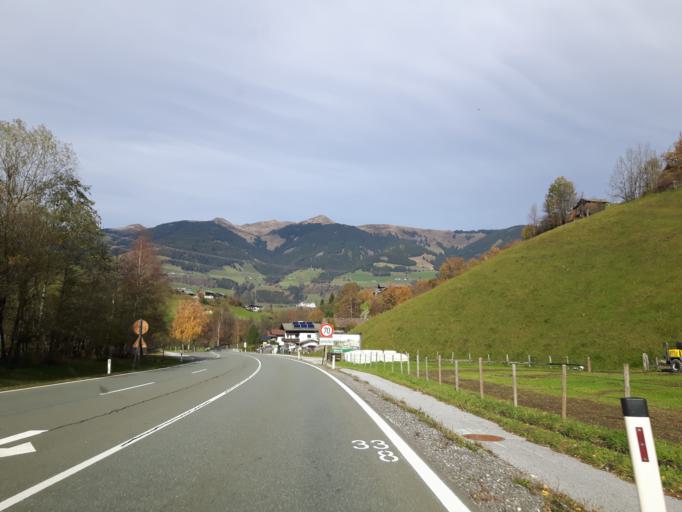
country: AT
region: Salzburg
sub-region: Politischer Bezirk Zell am See
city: Mittersill
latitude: 47.2844
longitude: 12.4909
